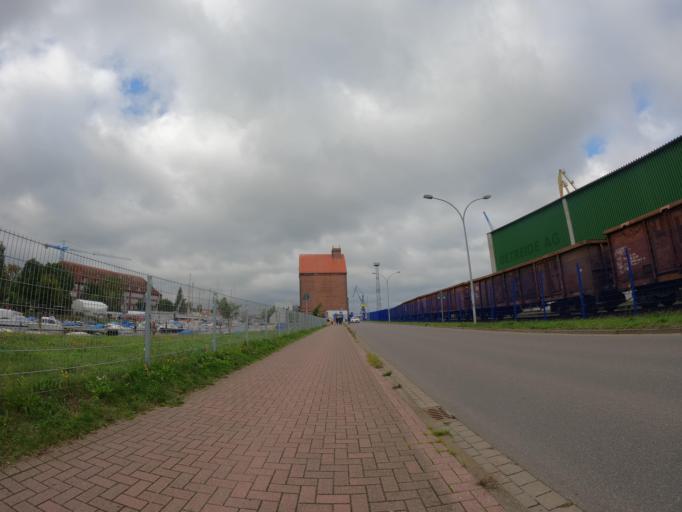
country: DE
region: Mecklenburg-Vorpommern
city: Stralsund
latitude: 54.3109
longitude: 13.1014
